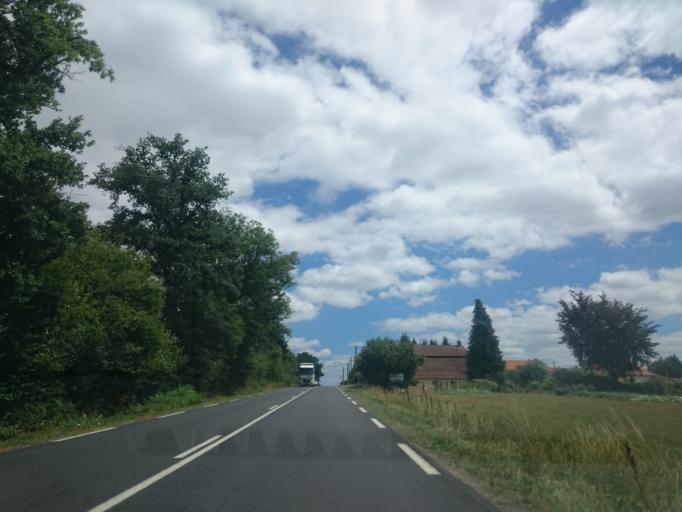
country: FR
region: Auvergne
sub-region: Departement du Cantal
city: Saint-Paul-des-Landes
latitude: 44.9486
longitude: 2.2996
